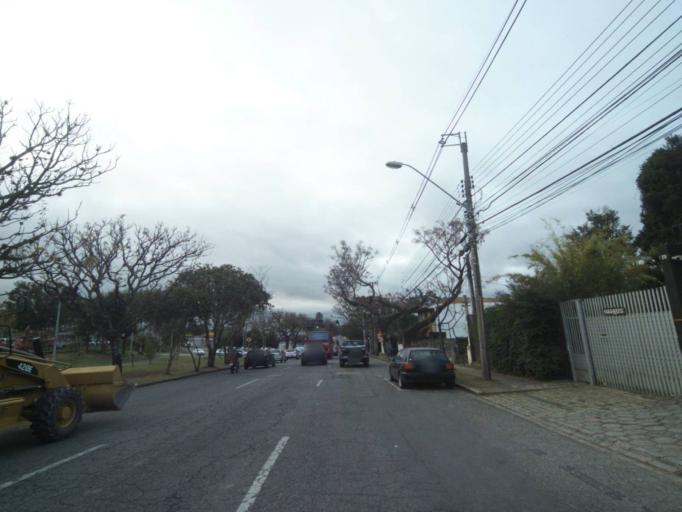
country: BR
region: Parana
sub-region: Curitiba
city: Curitiba
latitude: -25.4567
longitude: -49.2547
